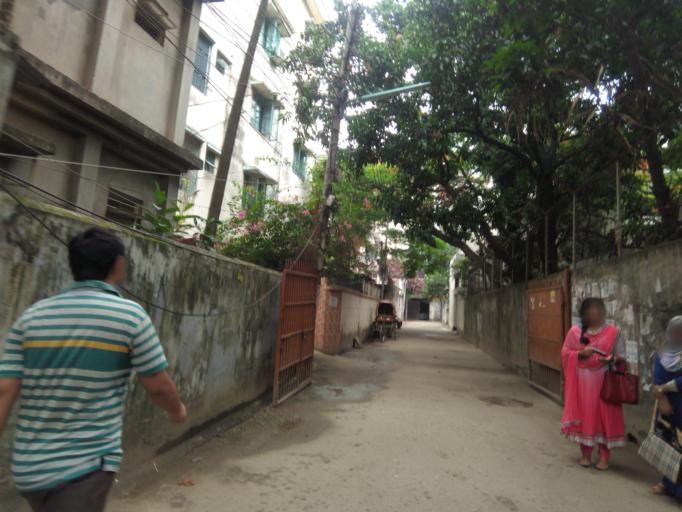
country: BD
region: Dhaka
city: Azimpur
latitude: 23.7564
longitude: 90.3829
